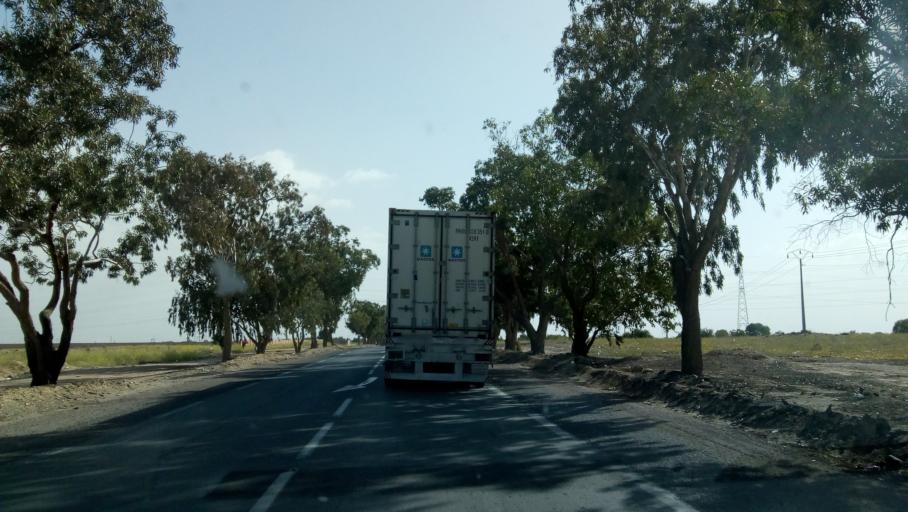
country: TN
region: Qabis
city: Gabes
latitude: 33.8913
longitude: 10.0319
